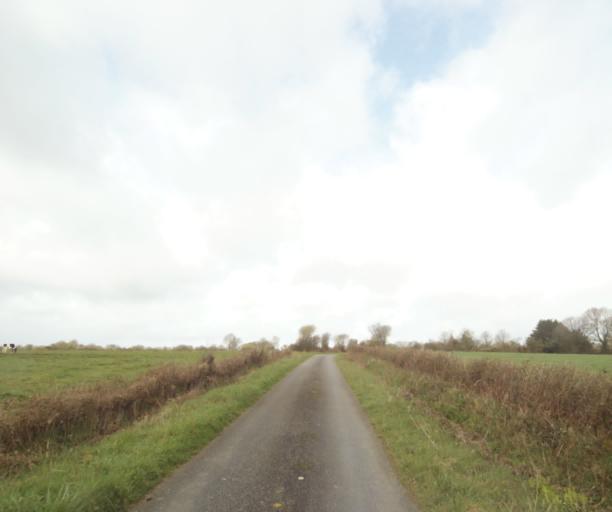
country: FR
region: Pays de la Loire
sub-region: Departement de la Loire-Atlantique
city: Bouvron
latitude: 47.4075
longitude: -1.8708
